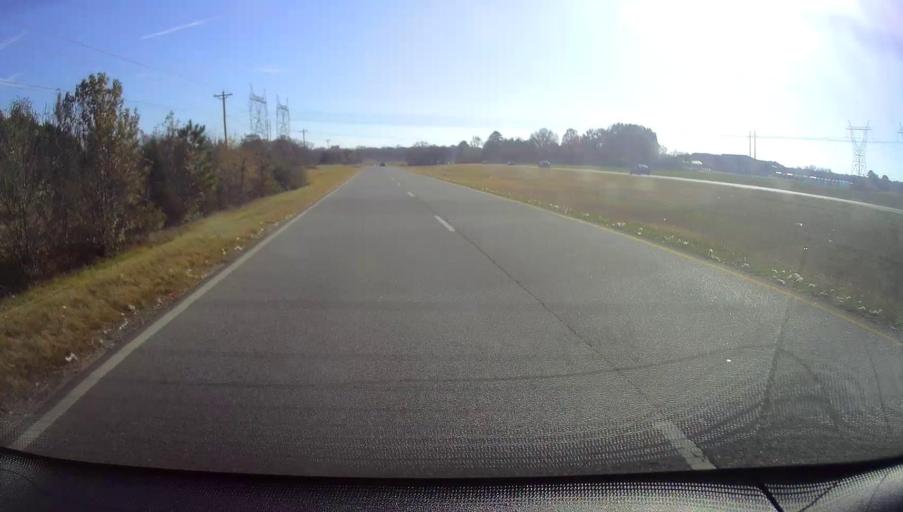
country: US
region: Alabama
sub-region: Morgan County
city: Decatur
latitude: 34.6976
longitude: -86.9556
